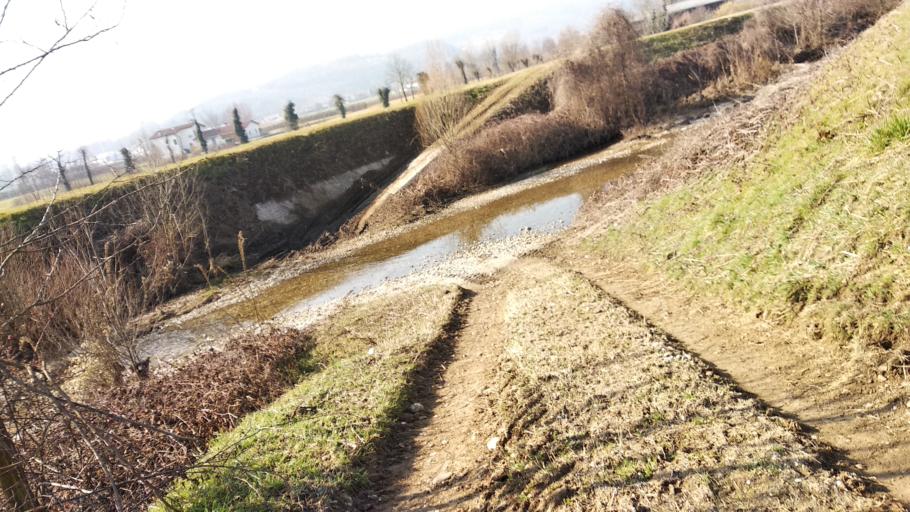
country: IT
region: Veneto
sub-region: Provincia di Vicenza
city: Motta
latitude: 45.5948
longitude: 11.4916
